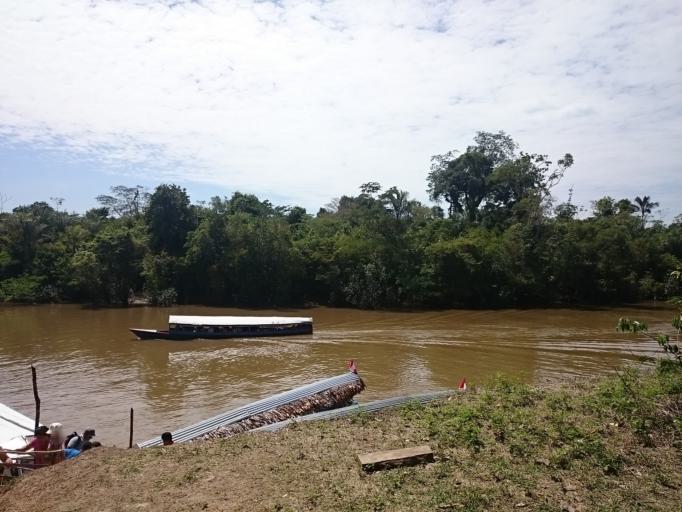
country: PE
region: Loreto
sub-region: Provincia de Maynas
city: Iquitos
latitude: -3.6853
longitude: -73.2811
